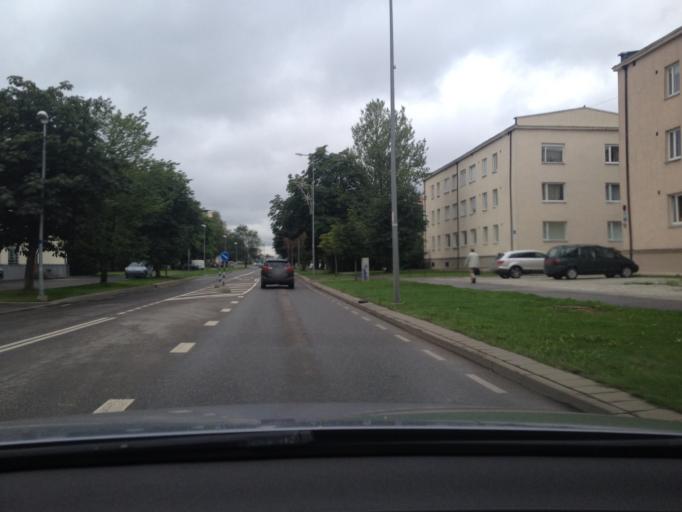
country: EE
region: Harju
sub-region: Tallinna linn
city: Tallinn
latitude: 59.4342
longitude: 24.8147
